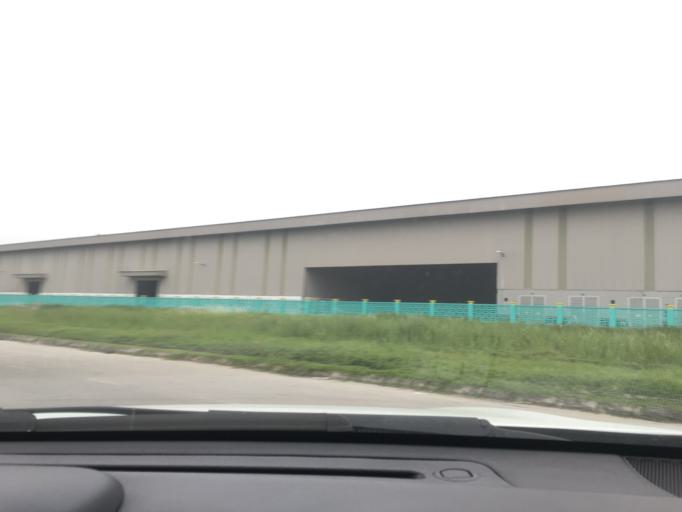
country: MY
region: Selangor
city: Klang
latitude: 3.1380
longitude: 101.4054
